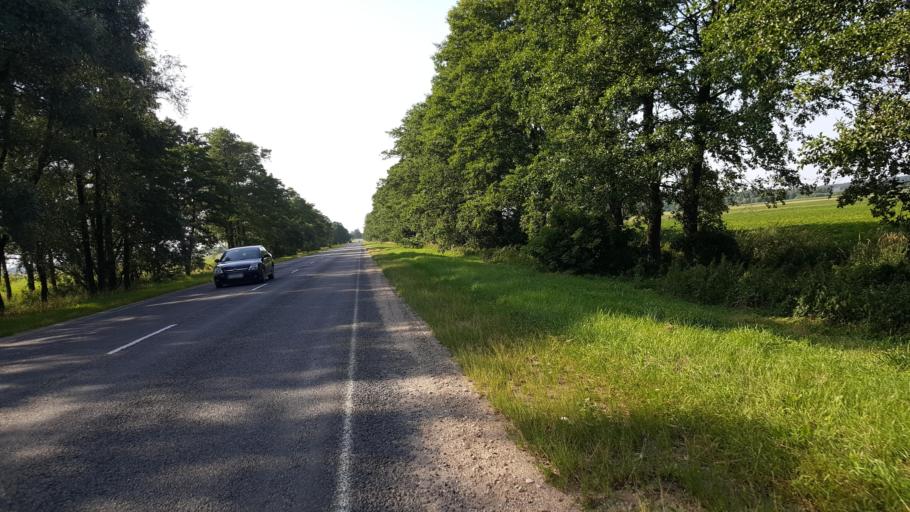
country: BY
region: Brest
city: Zhabinka
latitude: 52.3021
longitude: 23.9317
